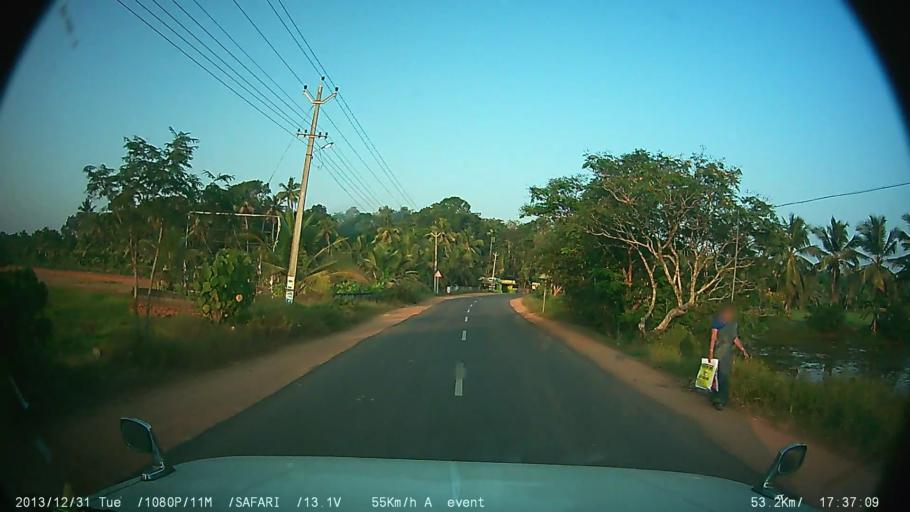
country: IN
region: Kerala
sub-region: Kottayam
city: Vaikam
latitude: 9.6945
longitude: 76.4762
